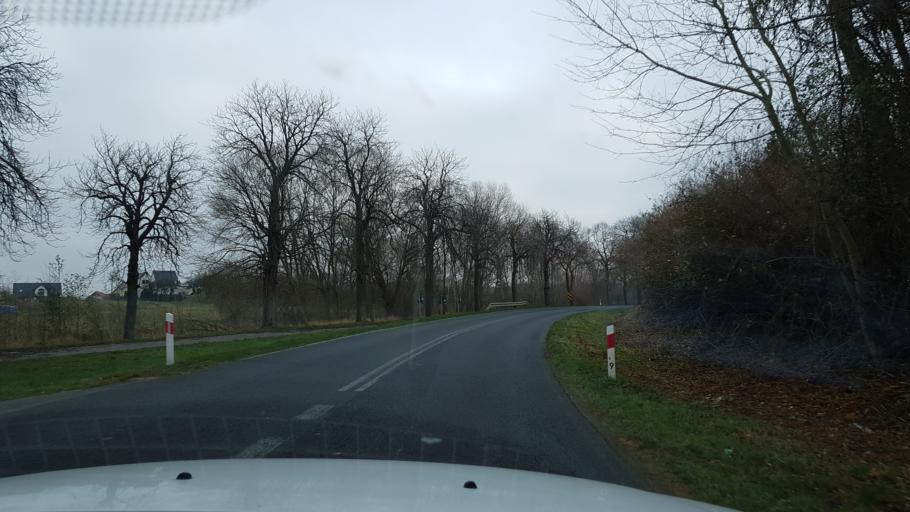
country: PL
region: West Pomeranian Voivodeship
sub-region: Powiat gryficki
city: Trzebiatow
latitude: 54.0685
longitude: 15.2485
